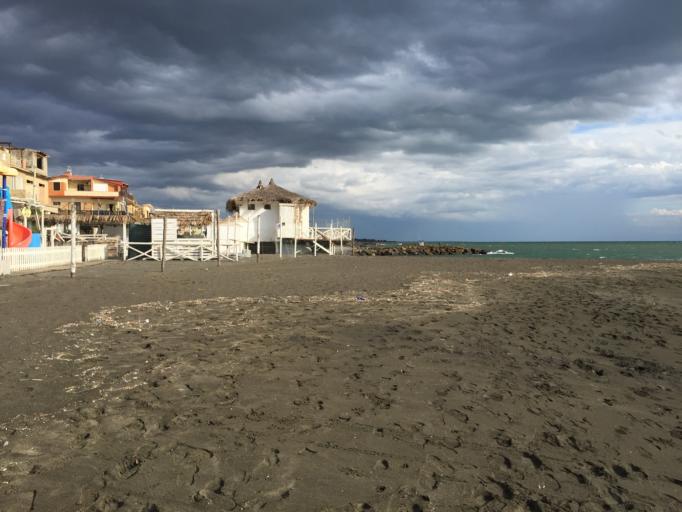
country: IT
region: Latium
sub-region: Citta metropolitana di Roma Capitale
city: Ladispoli
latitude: 41.9519
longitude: 12.0651
